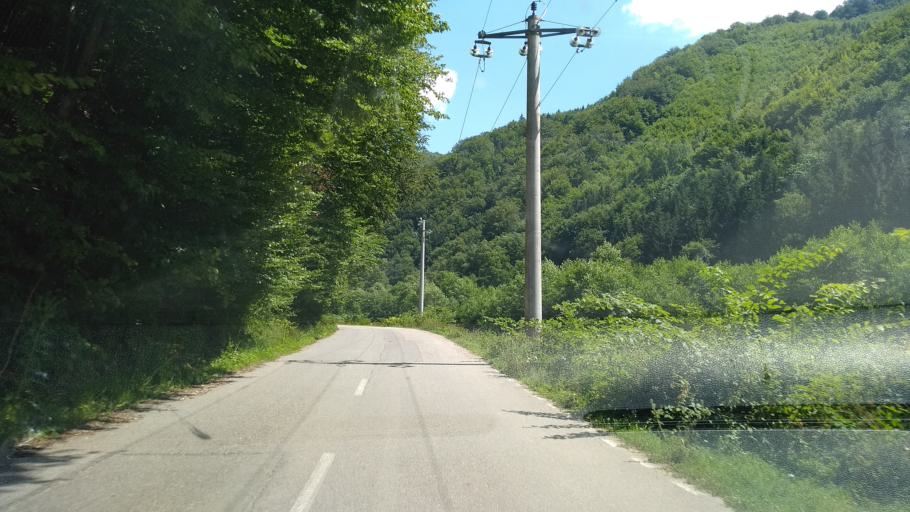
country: RO
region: Hunedoara
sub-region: Comuna Orastioara de Sus
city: Orastioara de Sus
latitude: 45.6215
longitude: 23.2307
